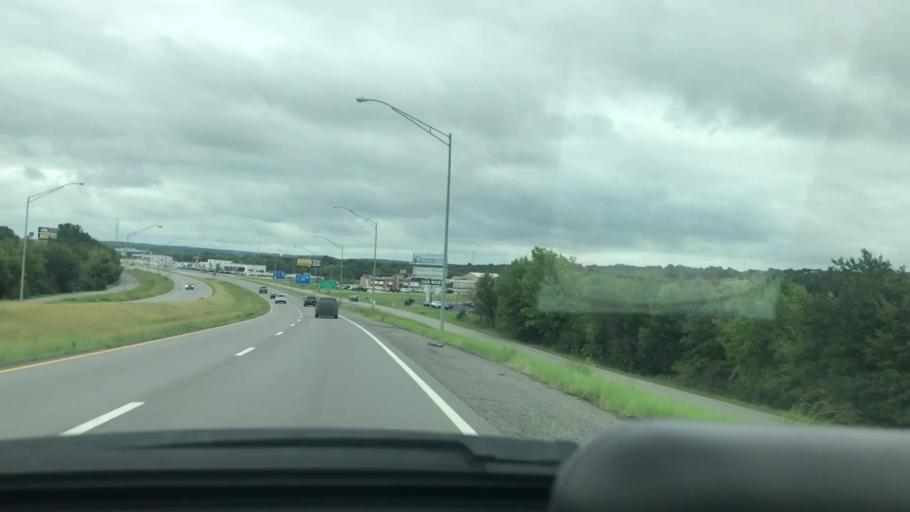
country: US
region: Oklahoma
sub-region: Pittsburg County
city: McAlester
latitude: 34.9035
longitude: -95.7473
